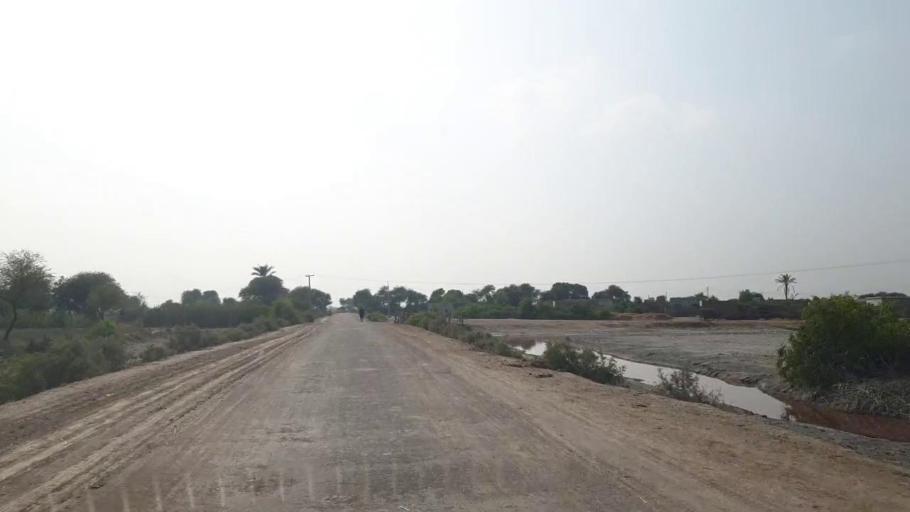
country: PK
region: Sindh
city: Rajo Khanani
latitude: 25.0270
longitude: 68.8033
